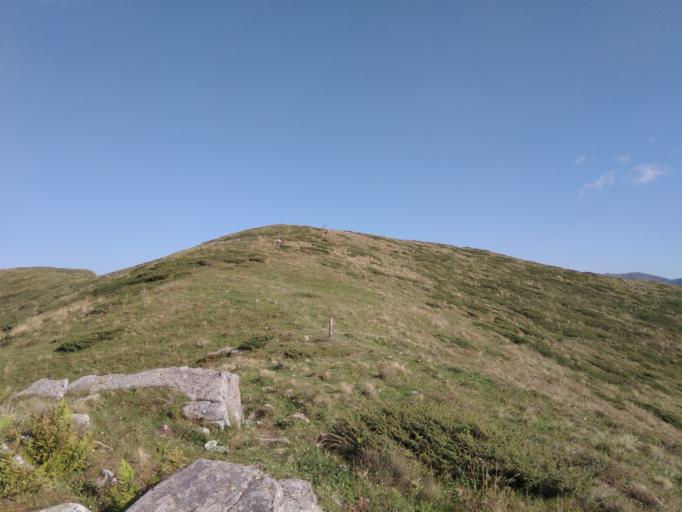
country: BG
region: Stara Zagora
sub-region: Obshtina Pavel Banya
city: Asen
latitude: 42.7617
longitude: 25.1013
